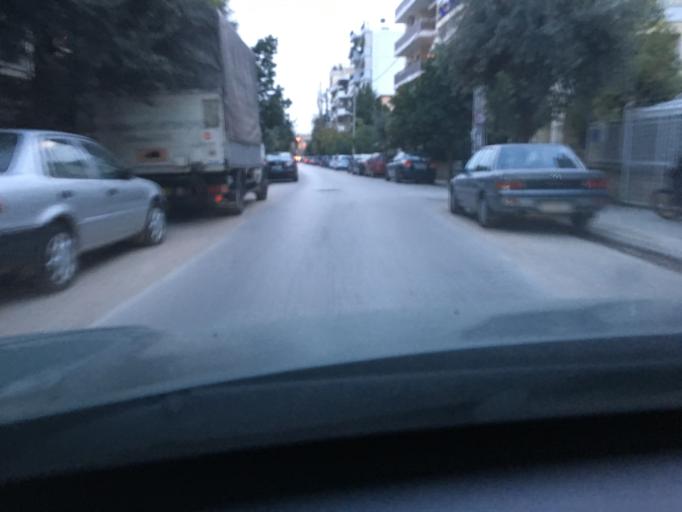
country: GR
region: Attica
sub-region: Nomarchia Athinas
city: Nea Chalkidona
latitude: 38.0302
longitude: 23.7313
